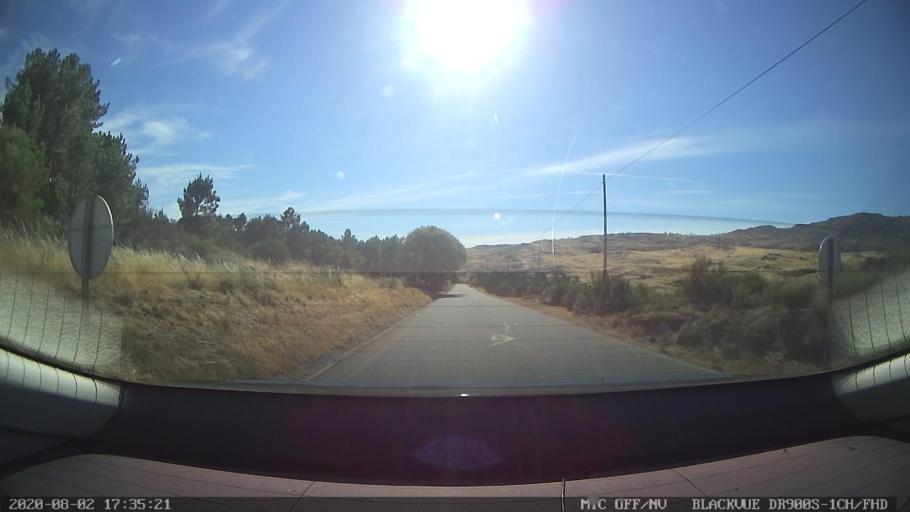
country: PT
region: Vila Real
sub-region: Murca
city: Murca
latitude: 41.3778
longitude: -7.5472
